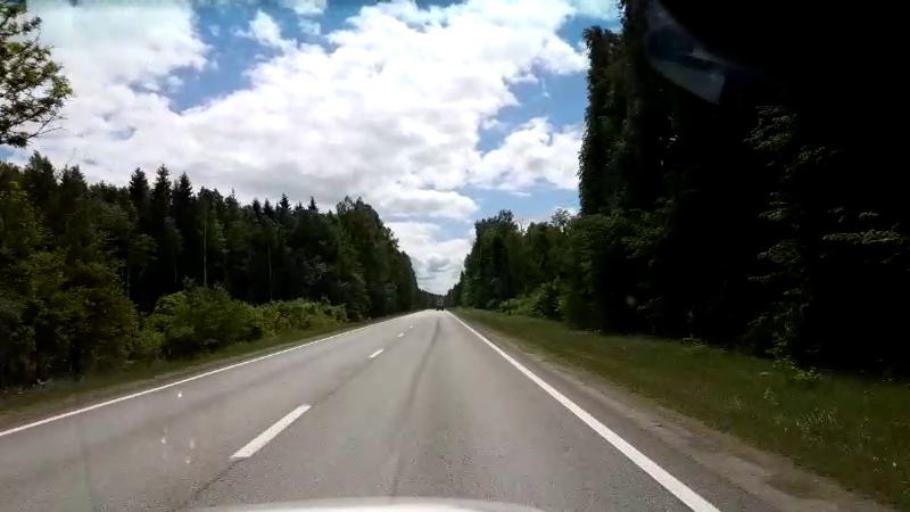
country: LV
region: Salacgrivas
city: Salacgriva
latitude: 57.5838
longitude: 24.4261
